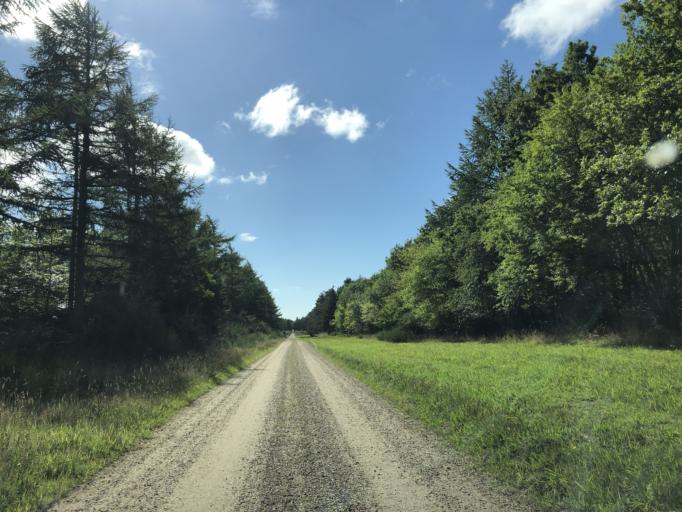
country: DK
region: Central Jutland
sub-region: Holstebro Kommune
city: Ulfborg
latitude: 56.2291
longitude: 8.4815
